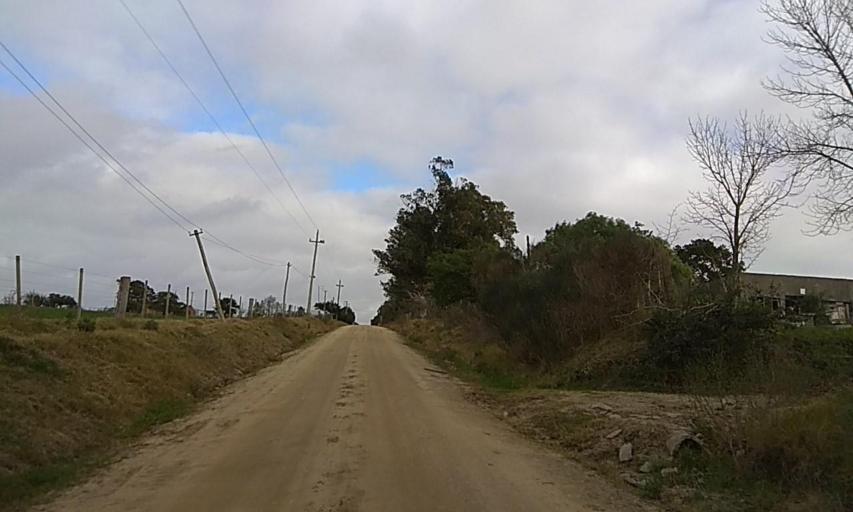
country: UY
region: Florida
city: Florida
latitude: -34.0619
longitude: -56.2020
